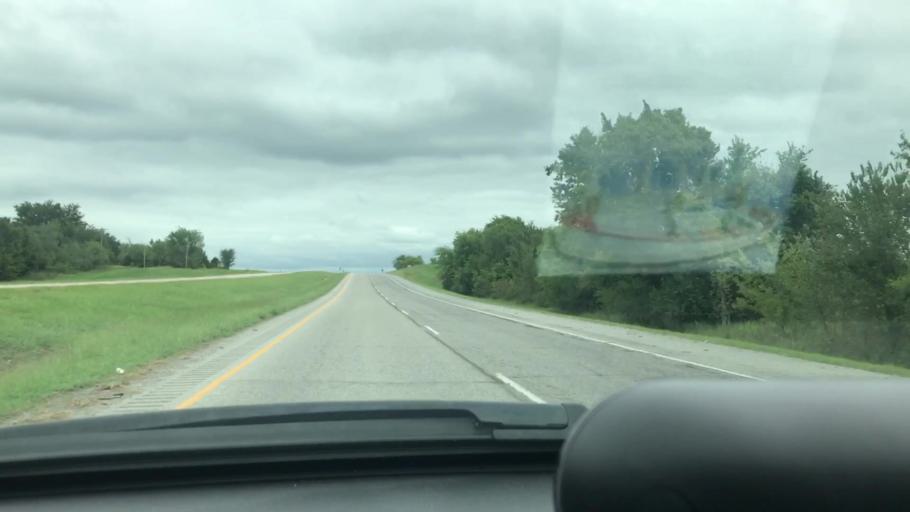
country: US
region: Oklahoma
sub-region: Wagoner County
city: Wagoner
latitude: 35.9885
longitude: -95.3741
